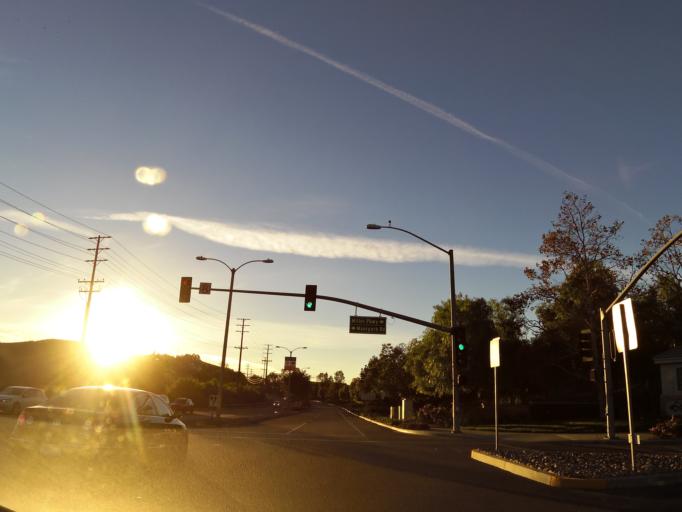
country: US
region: California
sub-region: Ventura County
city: Moorpark
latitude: 34.2638
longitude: -118.8608
